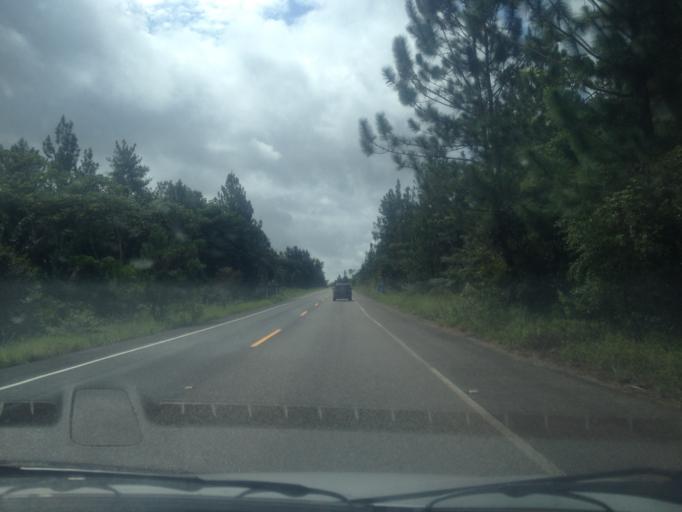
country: BR
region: Bahia
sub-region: Entre Rios
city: Entre Rios
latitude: -12.1466
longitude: -37.7959
